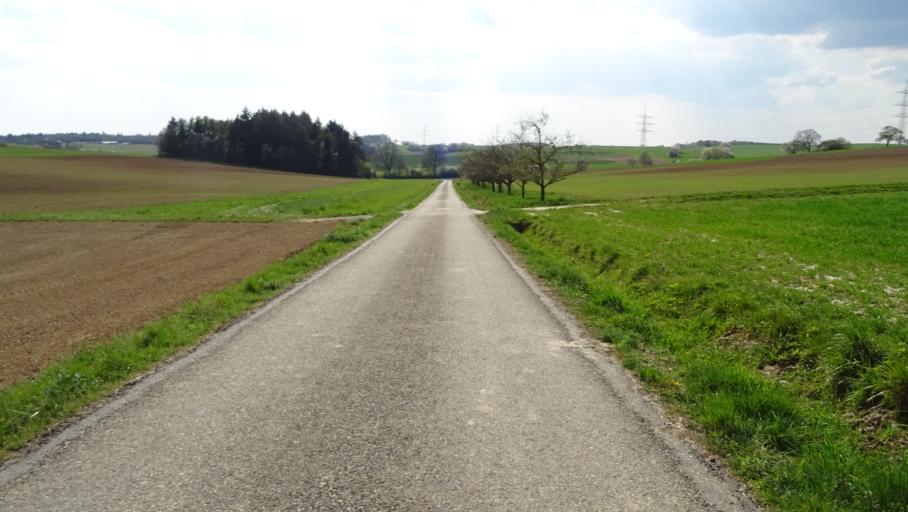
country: DE
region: Baden-Wuerttemberg
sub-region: Karlsruhe Region
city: Billigheim
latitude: 49.3892
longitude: 9.2520
